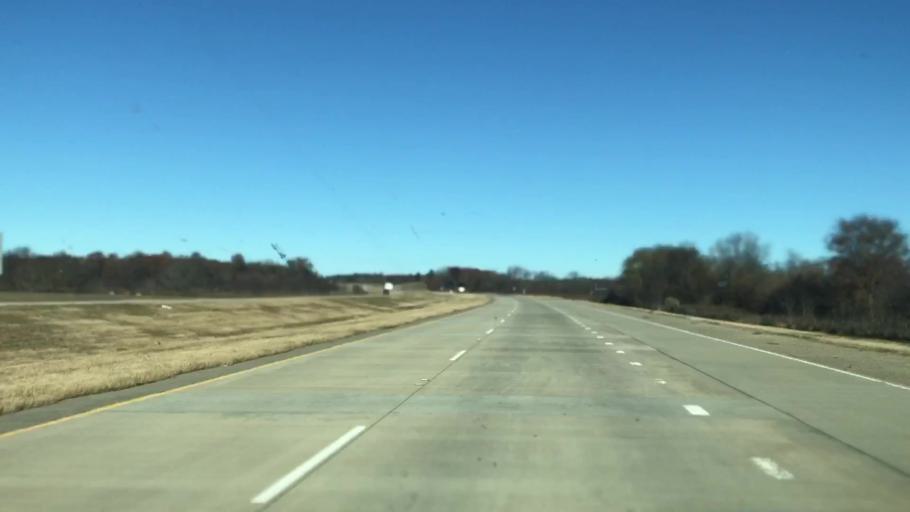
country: US
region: Louisiana
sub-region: Caddo Parish
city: Vivian
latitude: 32.9041
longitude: -93.8647
